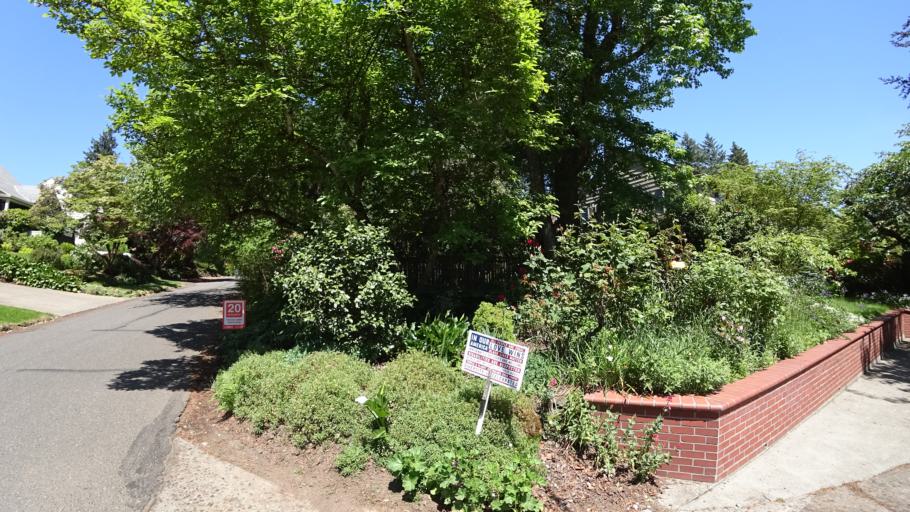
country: US
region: Oregon
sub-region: Multnomah County
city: Portland
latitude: 45.4772
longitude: -122.6879
